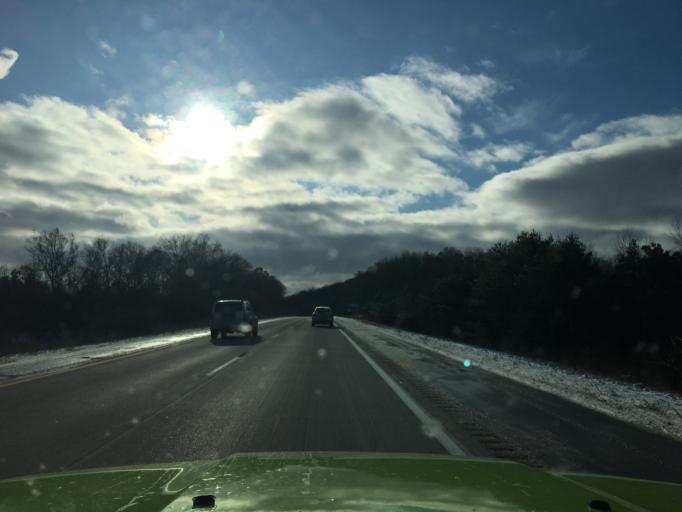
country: US
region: Michigan
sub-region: Kent County
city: Rockford
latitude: 43.1302
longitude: -85.5979
